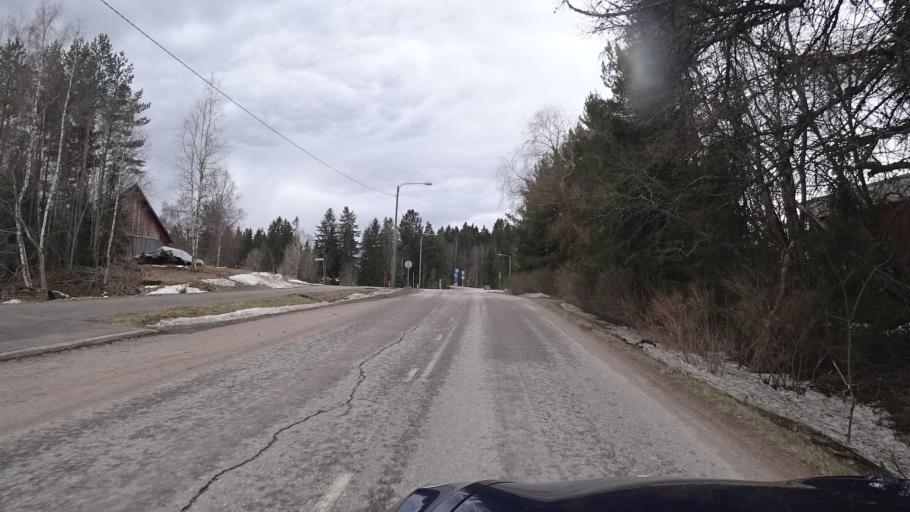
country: FI
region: Paijanne Tavastia
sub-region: Lahti
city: Nastola
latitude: 60.8679
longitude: 26.0112
